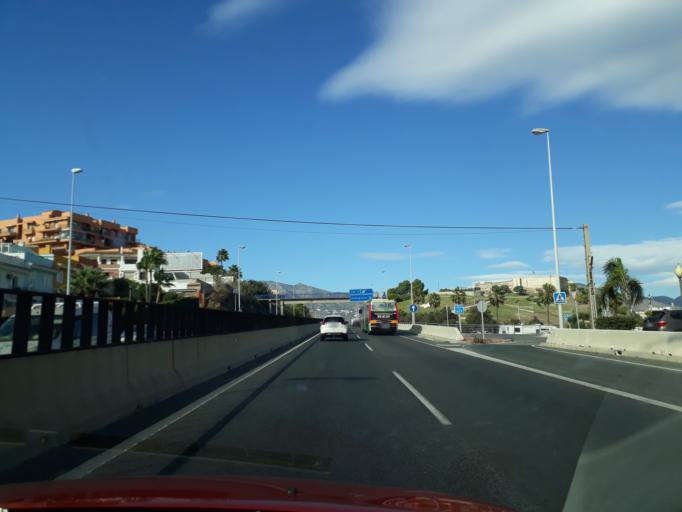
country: ES
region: Andalusia
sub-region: Provincia de Malaga
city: Fuengirola
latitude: 36.5220
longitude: -4.6302
